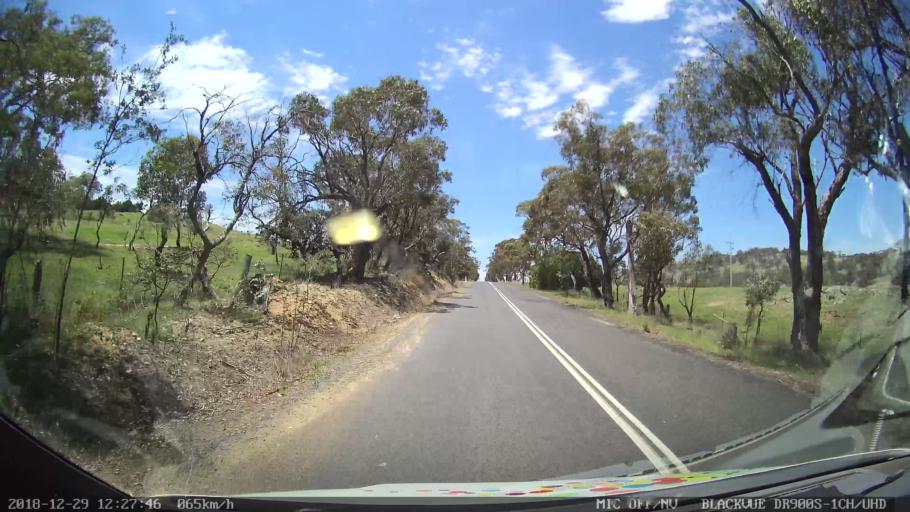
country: AU
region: Australian Capital Territory
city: Macarthur
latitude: -35.4800
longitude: 149.2242
